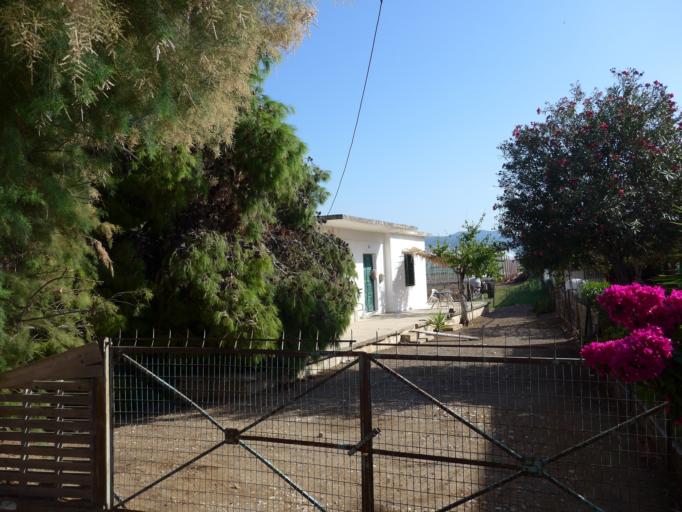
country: GR
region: Peloponnese
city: Asklipieio
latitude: 37.4932
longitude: 22.9913
